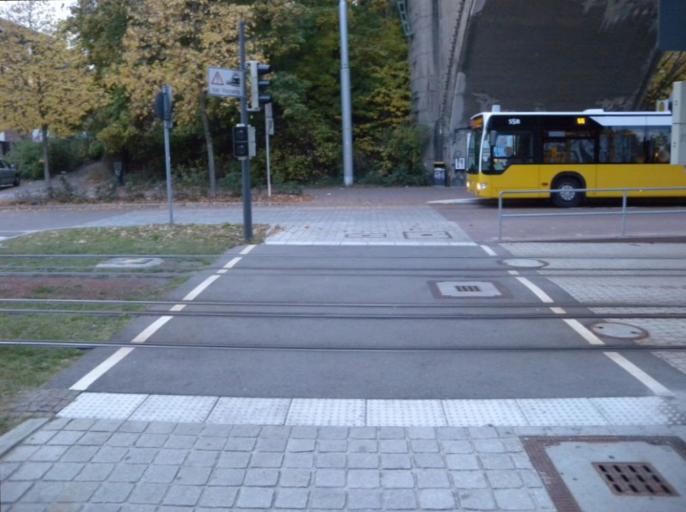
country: DE
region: Baden-Wuerttemberg
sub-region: Regierungsbezirk Stuttgart
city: Stuttgart
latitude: 48.8025
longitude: 9.1900
